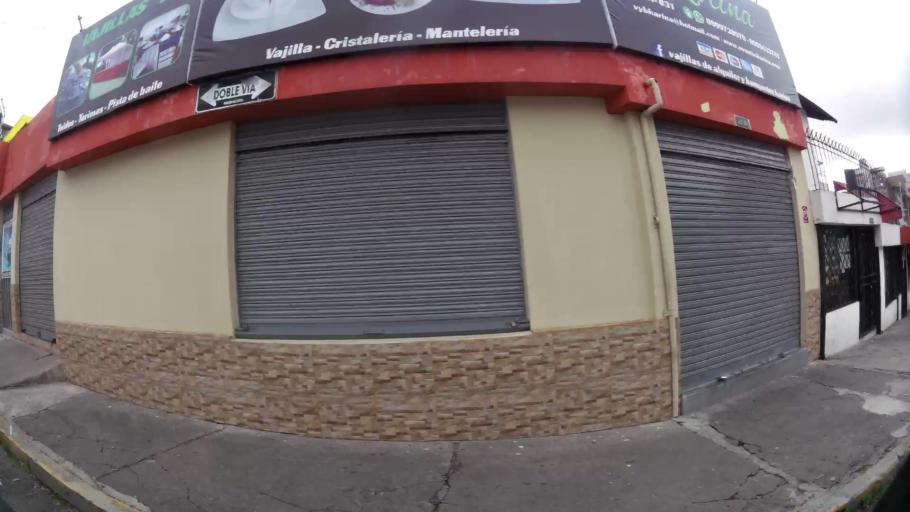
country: EC
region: Pichincha
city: Quito
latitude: -0.1866
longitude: -78.4904
